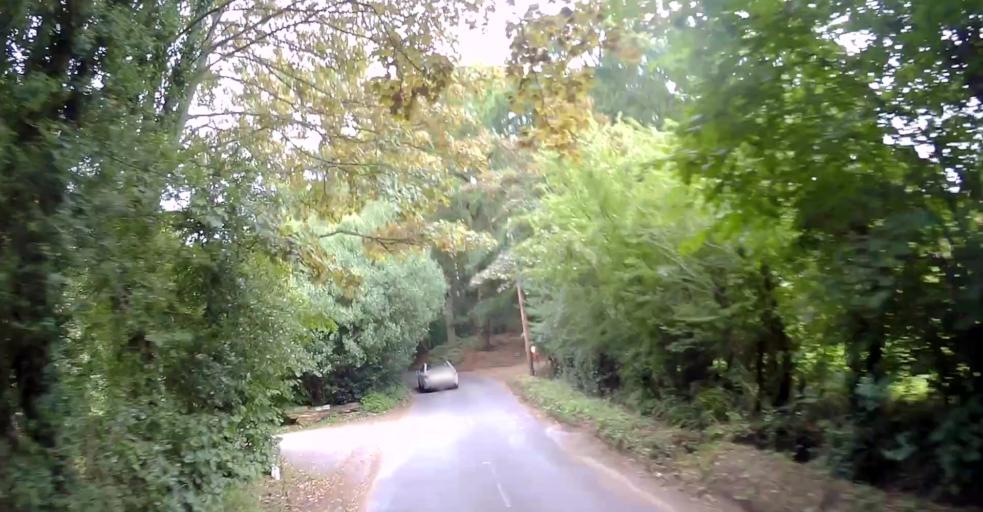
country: GB
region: England
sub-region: Surrey
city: Hale
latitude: 51.2126
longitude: -0.7752
